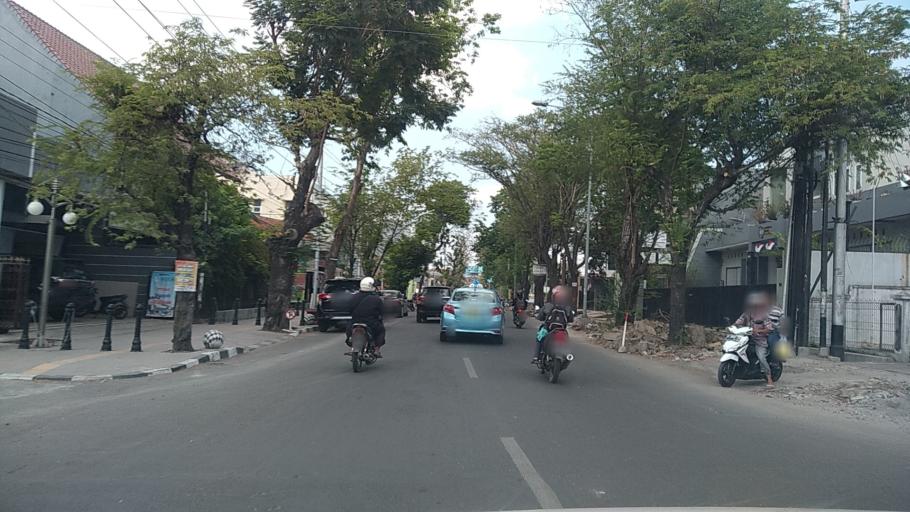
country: ID
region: Central Java
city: Semarang
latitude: -6.9797
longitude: 110.4044
